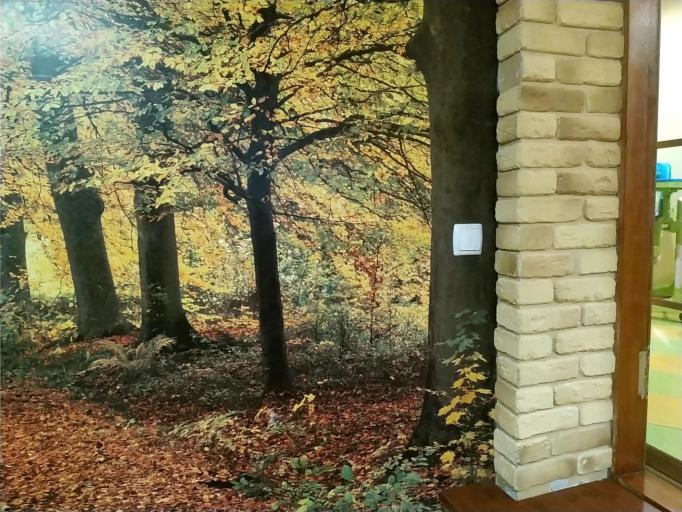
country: RU
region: Smolensk
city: Safonovo
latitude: 55.2032
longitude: 33.2451
